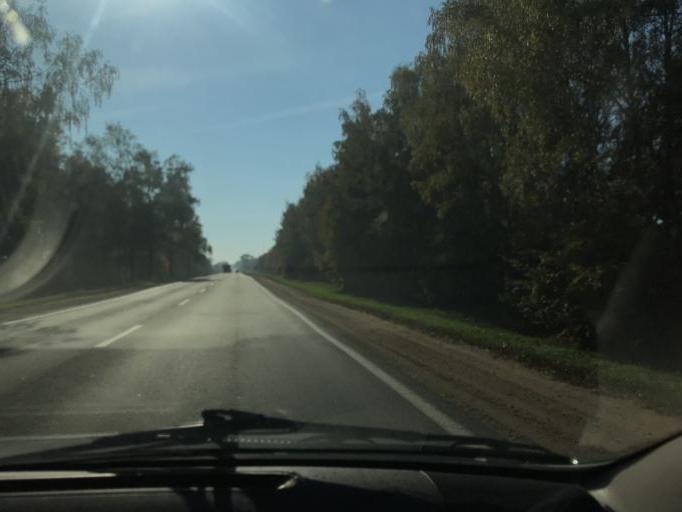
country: BY
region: Minsk
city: Salihorsk
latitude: 52.8088
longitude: 27.4649
